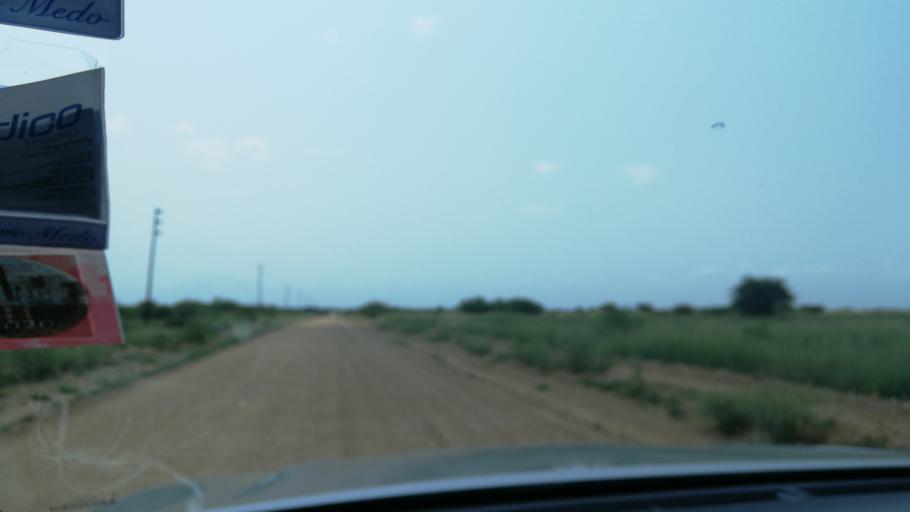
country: MZ
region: Maputo
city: Matola
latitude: -26.0739
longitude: 32.3908
